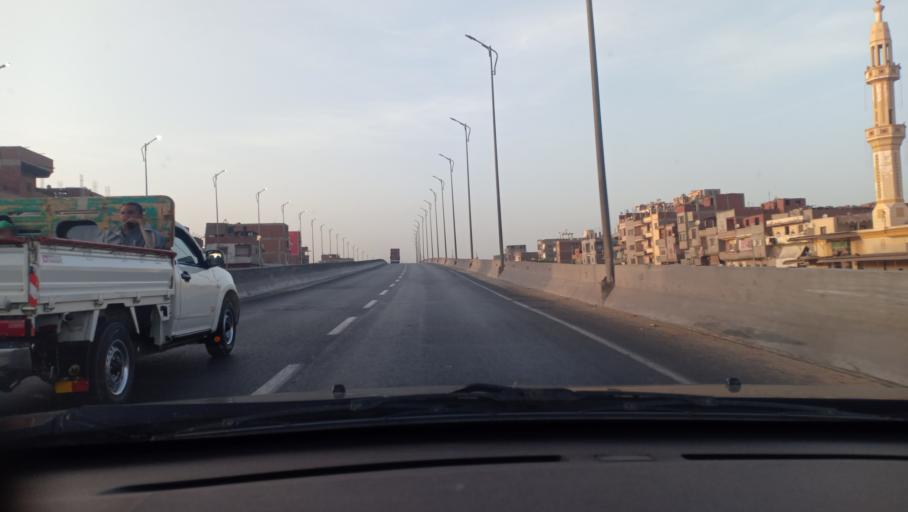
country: EG
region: Muhafazat al Gharbiyah
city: Zifta
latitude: 30.6352
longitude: 31.2804
